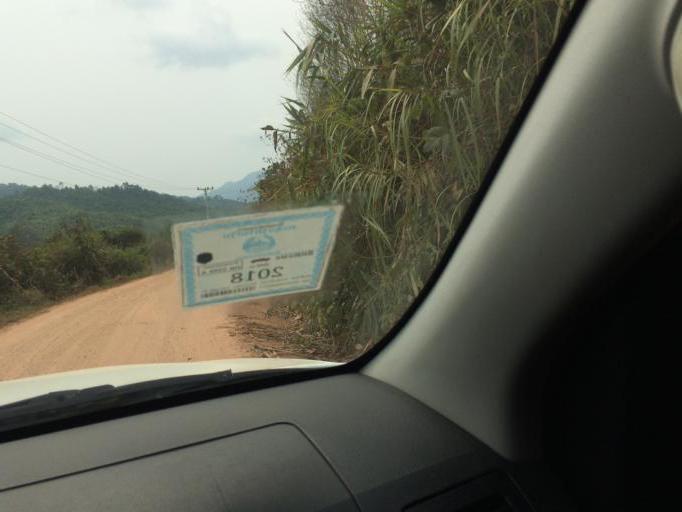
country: LA
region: Loungnamtha
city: Muang Nale
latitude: 20.2201
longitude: 101.6639
